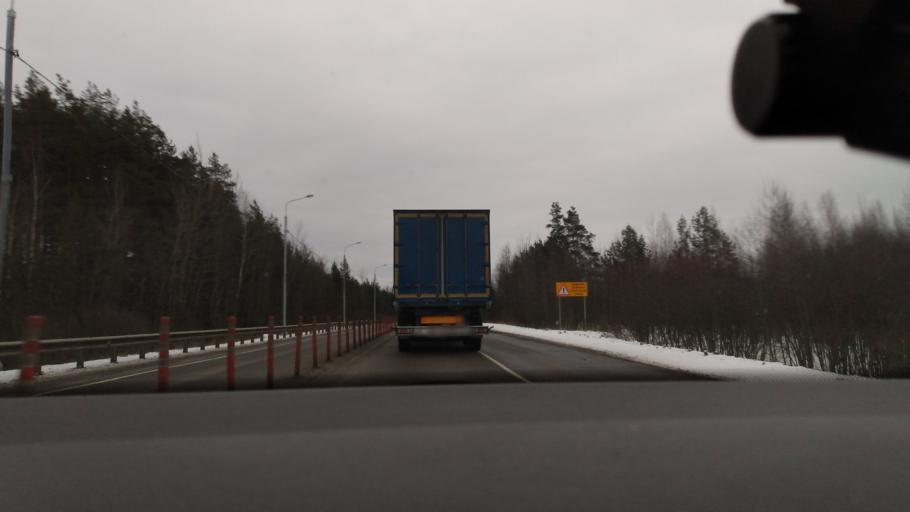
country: RU
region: Moskovskaya
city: Yegor'yevsk
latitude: 55.4476
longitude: 39.0105
